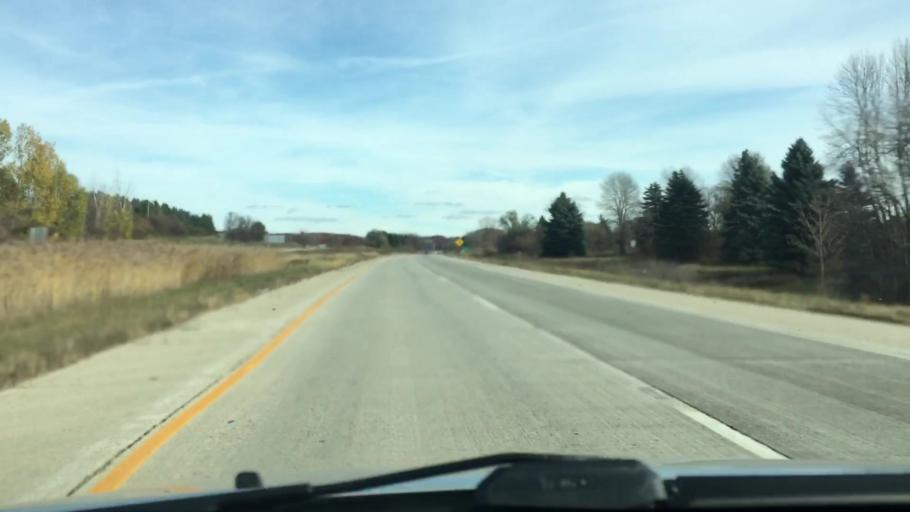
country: US
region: Wisconsin
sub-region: Brown County
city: Green Bay
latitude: 44.5250
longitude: -87.9382
